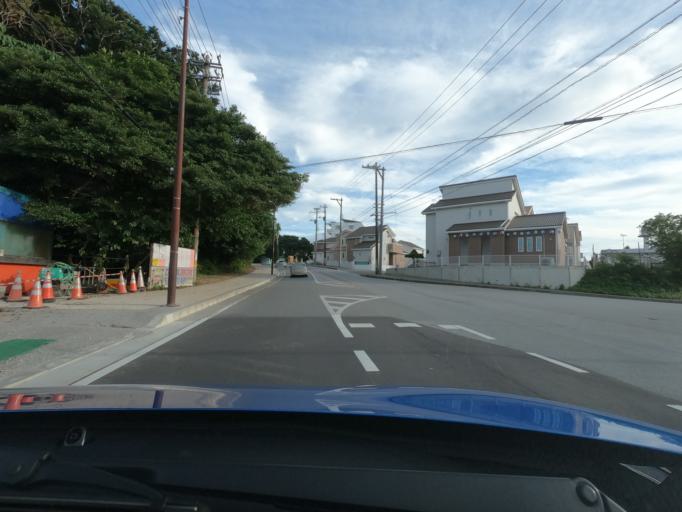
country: JP
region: Okinawa
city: Nago
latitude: 26.6785
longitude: 127.8883
